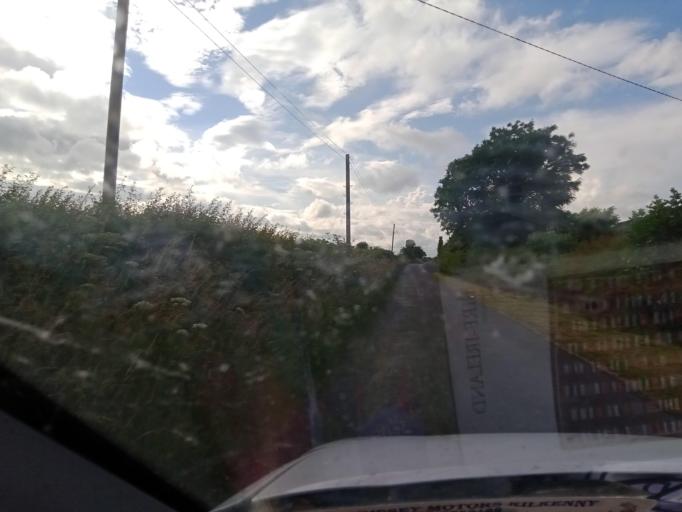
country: IE
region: Leinster
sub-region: Laois
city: Rathdowney
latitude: 52.7862
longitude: -7.5509
